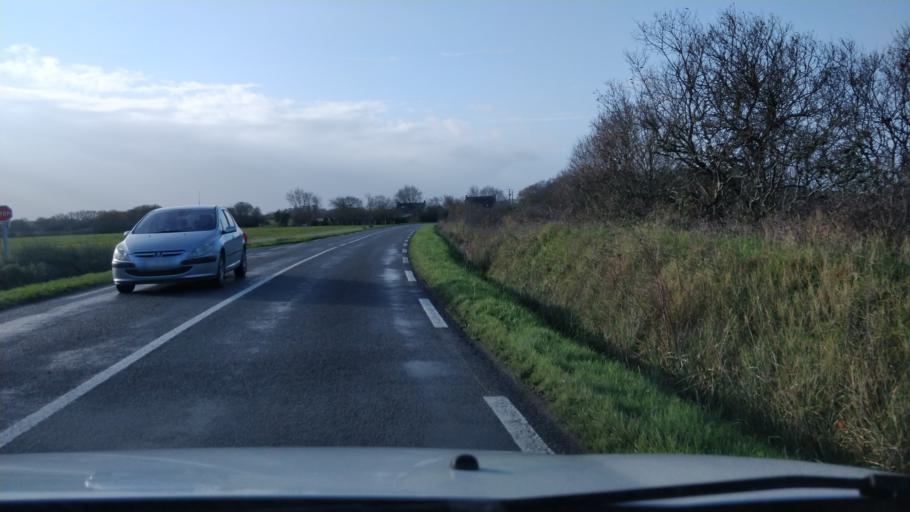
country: FR
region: Pays de la Loire
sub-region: Departement de la Loire-Atlantique
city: Asserac
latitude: 47.4057
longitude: -2.3997
